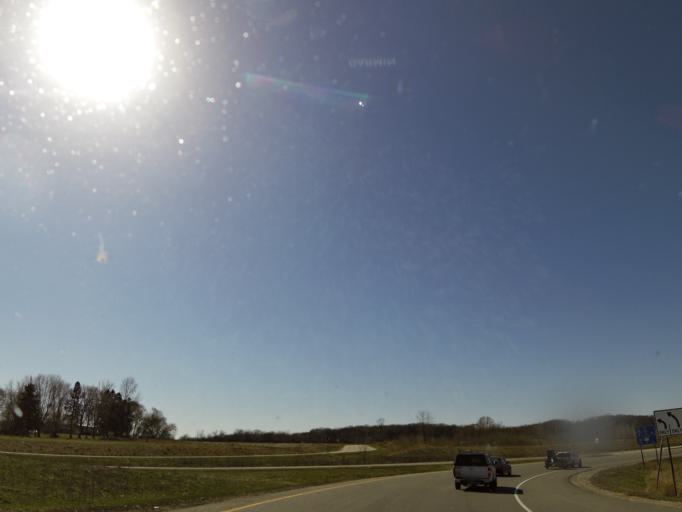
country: US
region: Minnesota
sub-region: Dakota County
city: Lakeville
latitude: 44.6433
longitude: -93.2978
